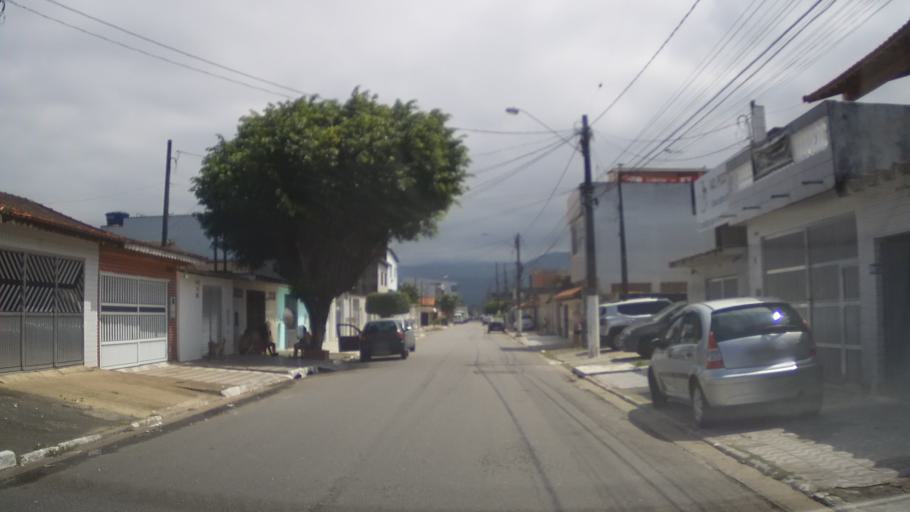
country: BR
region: Sao Paulo
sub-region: Praia Grande
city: Praia Grande
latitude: -24.0188
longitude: -46.4829
